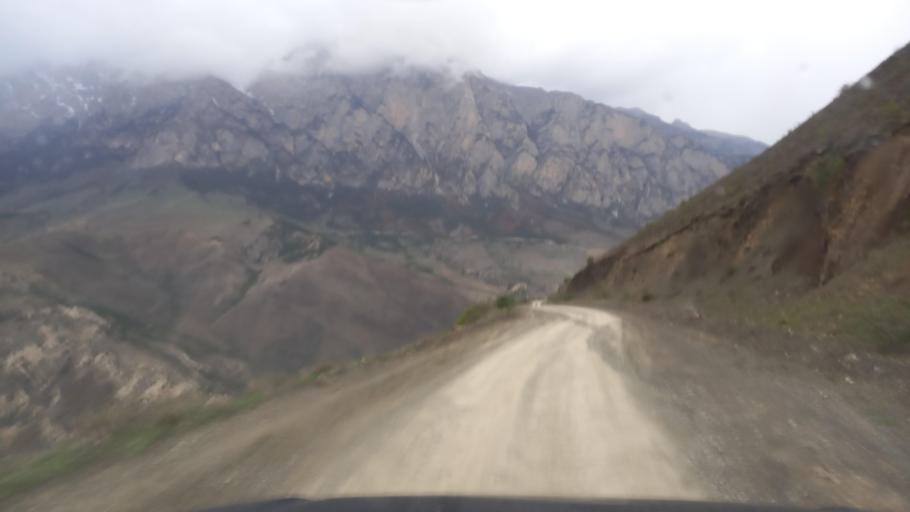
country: RU
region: North Ossetia
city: Mizur
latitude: 42.8561
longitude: 44.1598
